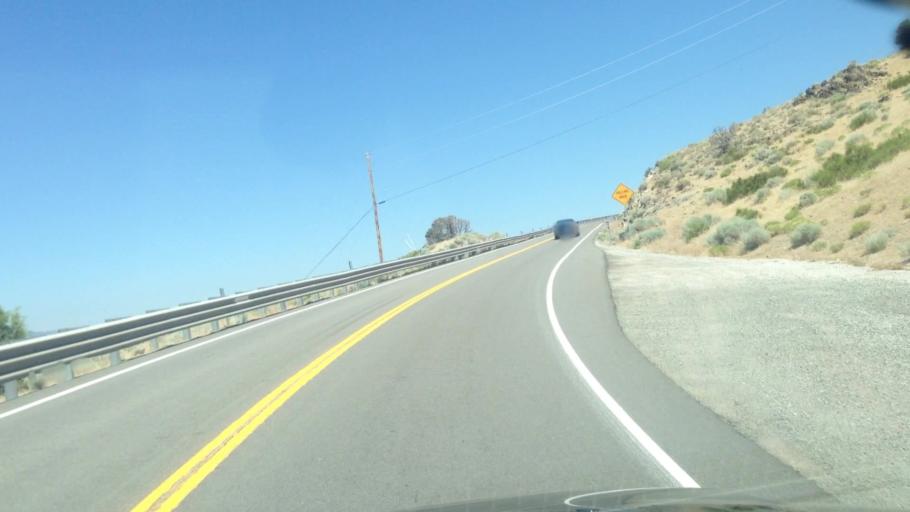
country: US
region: Nevada
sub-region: Storey County
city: Virginia City
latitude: 39.3899
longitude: -119.7096
